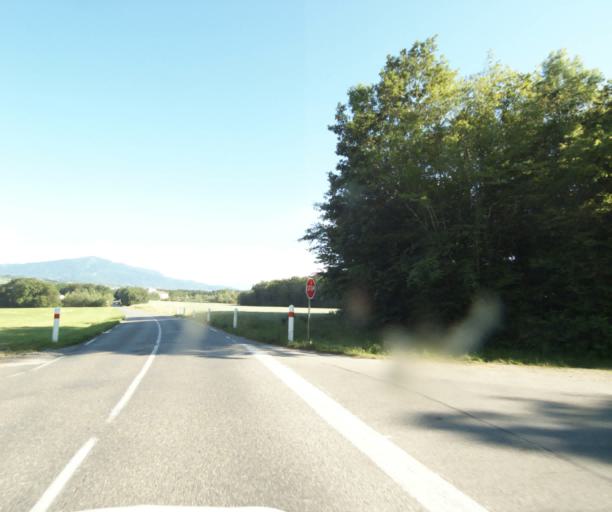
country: FR
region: Rhone-Alpes
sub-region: Departement de la Haute-Savoie
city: Douvaine
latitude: 46.3259
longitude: 6.2925
